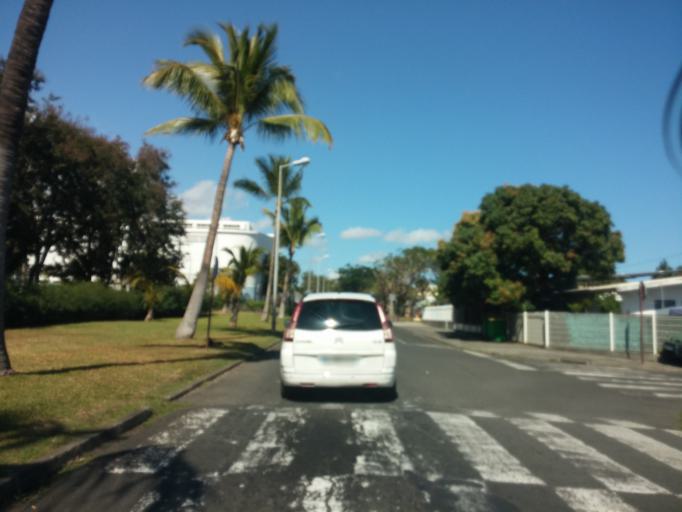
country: RE
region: Reunion
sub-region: Reunion
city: Le Port
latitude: -20.9486
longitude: 55.2931
